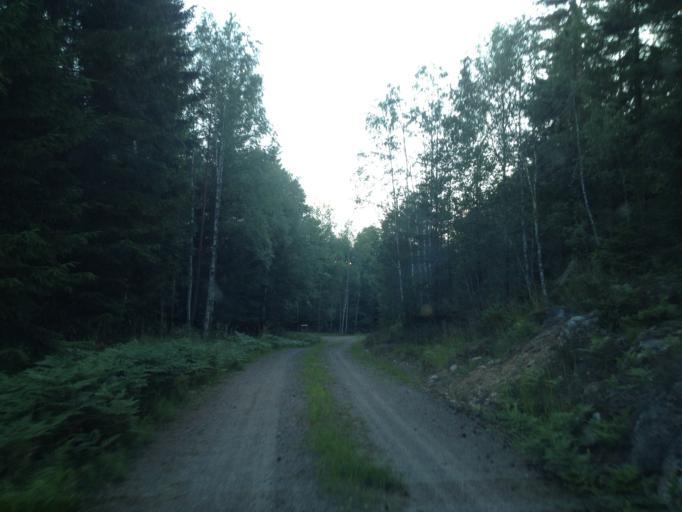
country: SE
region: Kalmar
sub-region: Vasterviks Kommun
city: Overum
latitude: 57.9976
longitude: 16.1382
